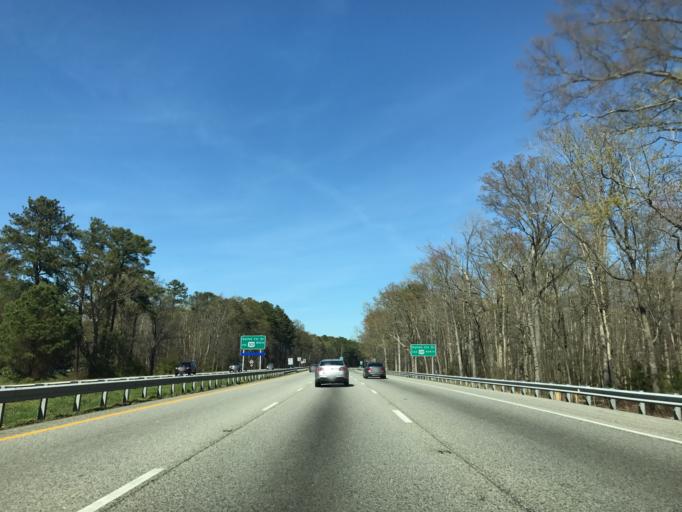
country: US
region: Maryland
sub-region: Queen Anne's County
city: Grasonville
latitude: 38.9763
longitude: -76.1731
